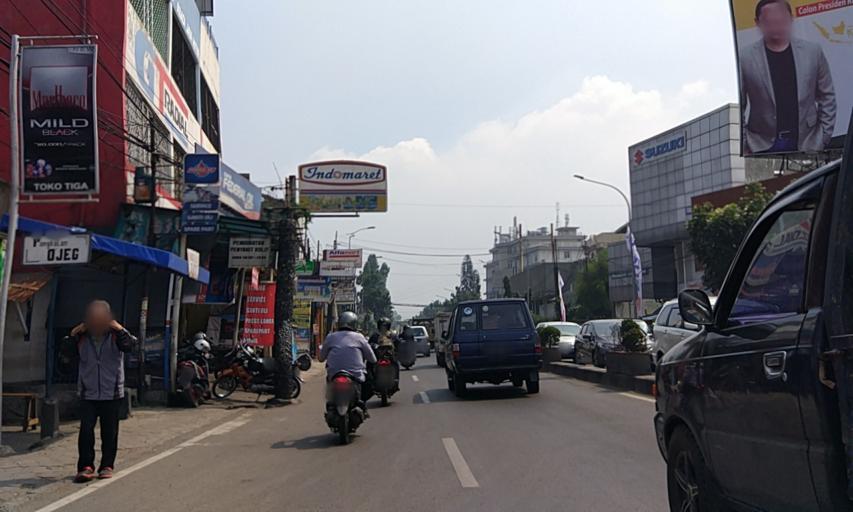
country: ID
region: West Java
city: Cimahi
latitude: -6.9103
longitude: 107.5689
